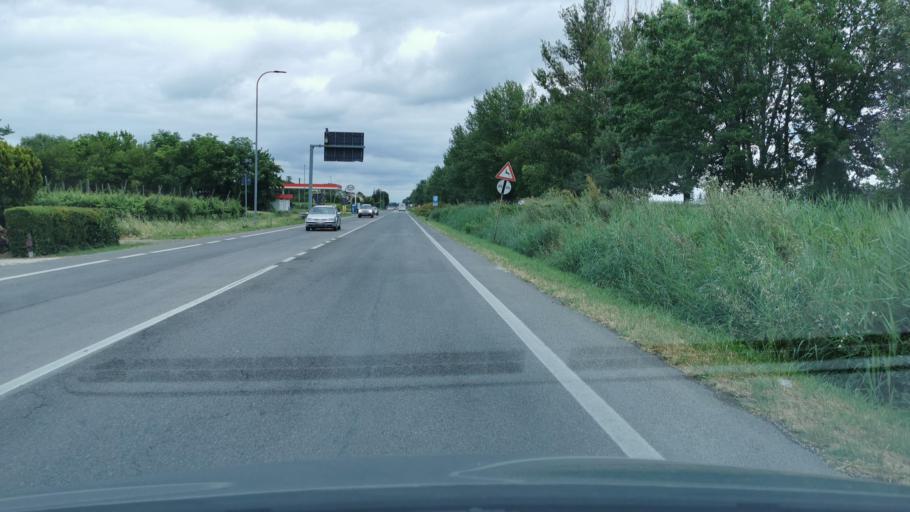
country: IT
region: Emilia-Romagna
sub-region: Provincia di Ravenna
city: Granarolo
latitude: 44.3276
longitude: 11.9098
